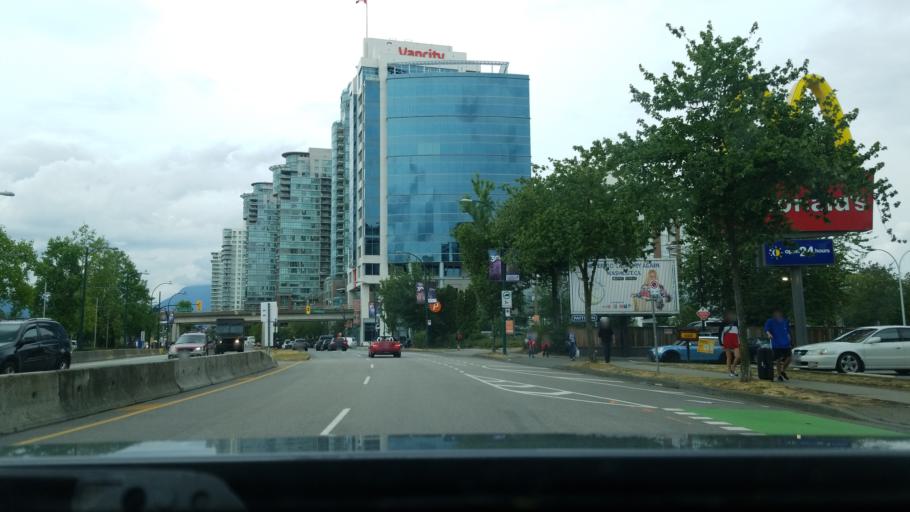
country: CA
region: British Columbia
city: Vancouver
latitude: 49.2720
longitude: -123.1018
